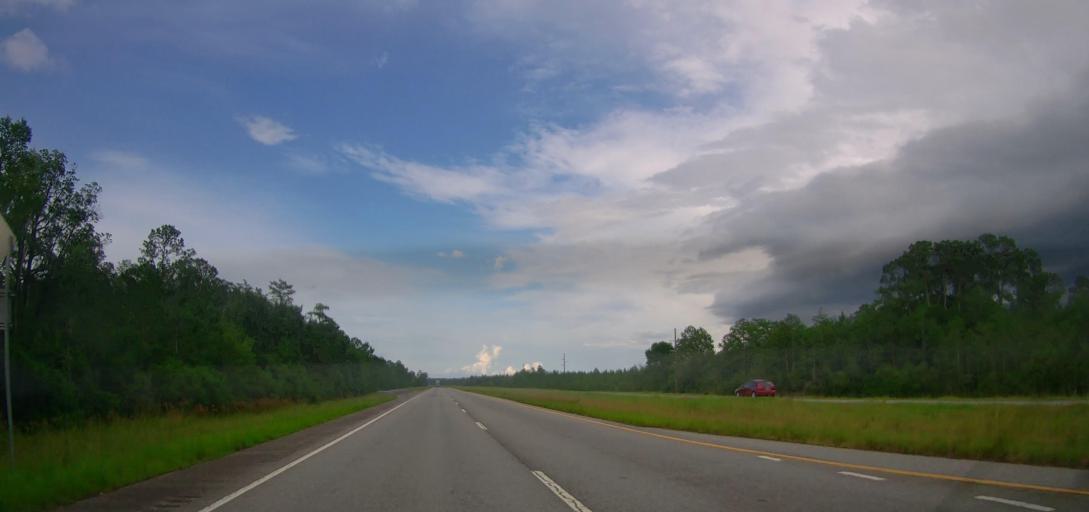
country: US
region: Georgia
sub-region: Pierce County
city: Blackshear
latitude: 31.4419
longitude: -82.0764
